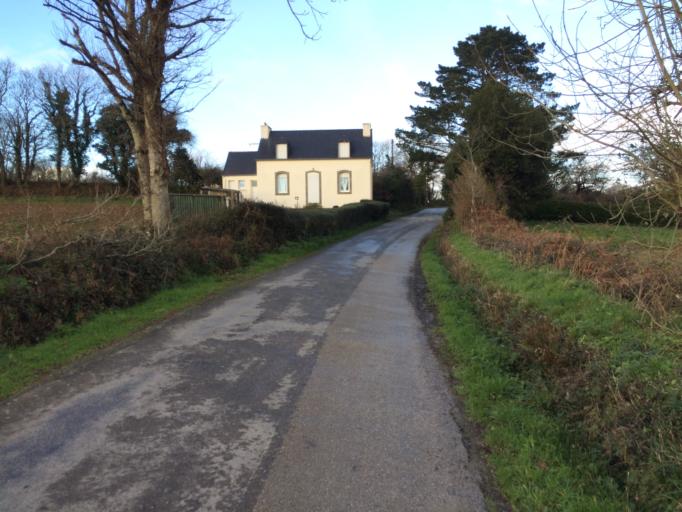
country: FR
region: Brittany
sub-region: Departement du Finistere
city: Logonna-Daoulas
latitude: 48.3333
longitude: -4.2702
